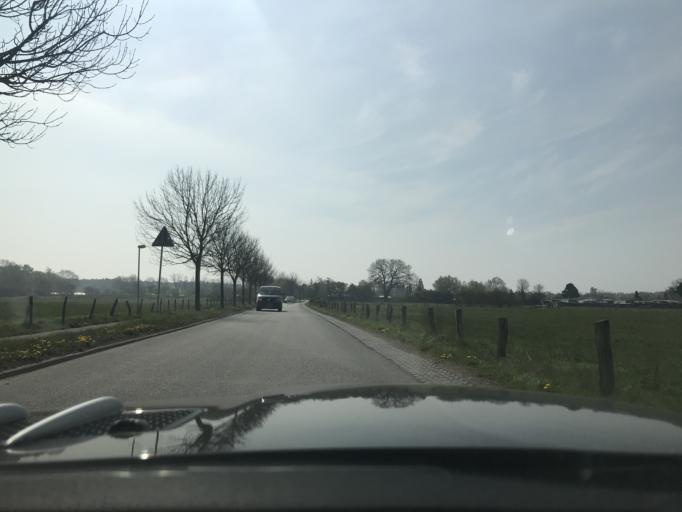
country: DE
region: Schleswig-Holstein
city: Gromitz
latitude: 54.1628
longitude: 10.9849
